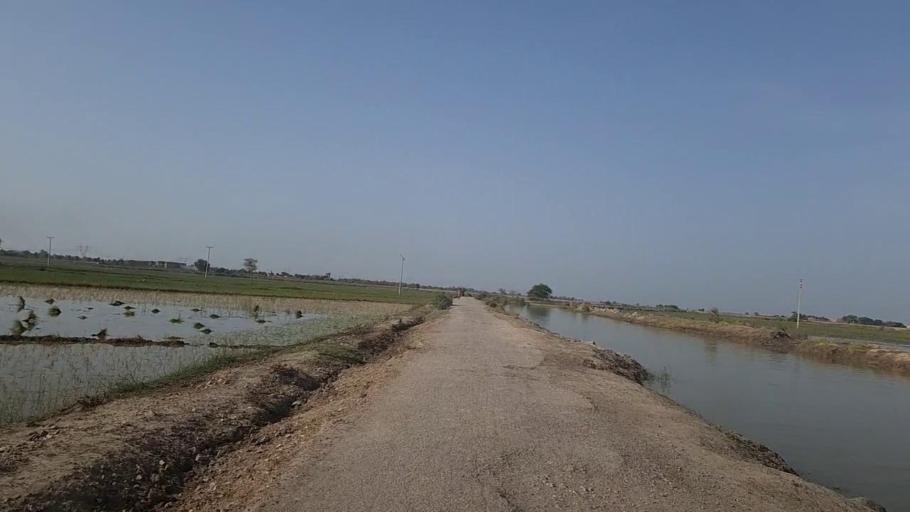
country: PK
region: Sindh
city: Sita Road
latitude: 27.1124
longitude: 67.8771
